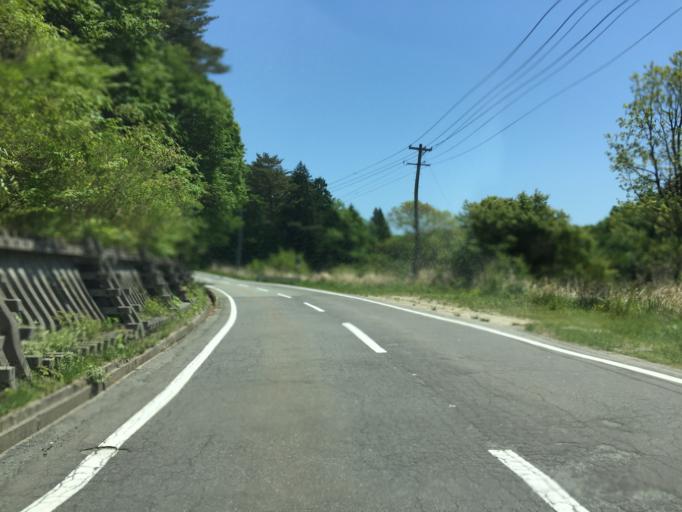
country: JP
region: Fukushima
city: Namie
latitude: 37.5241
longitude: 140.8084
